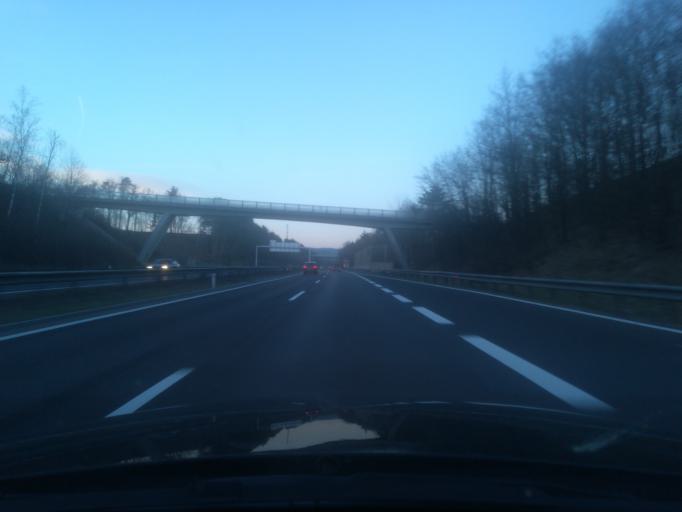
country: AT
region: Upper Austria
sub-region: Politischer Bezirk Urfahr-Umgebung
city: Engerwitzdorf
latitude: 48.3508
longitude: 14.4572
